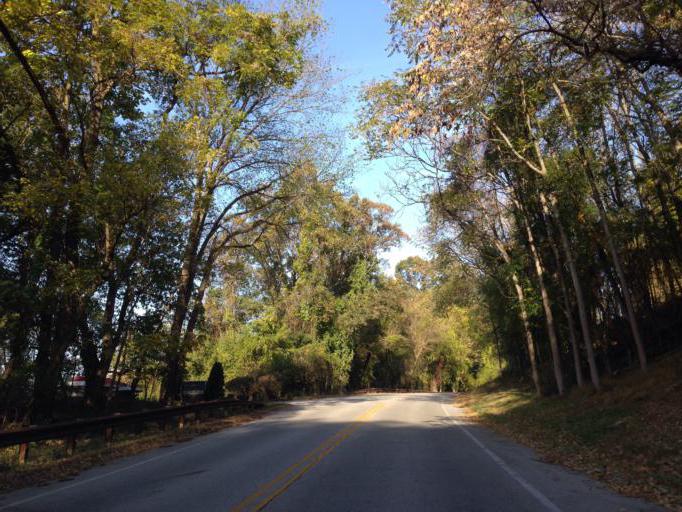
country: US
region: Maryland
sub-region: Howard County
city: Ellicott City
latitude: 39.2713
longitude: -76.7994
